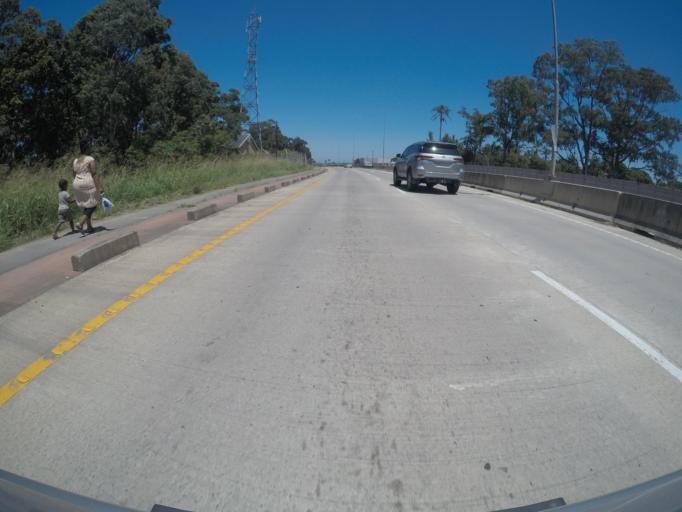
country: ZA
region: Eastern Cape
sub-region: Buffalo City Metropolitan Municipality
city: East London
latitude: -32.9391
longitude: 27.9780
